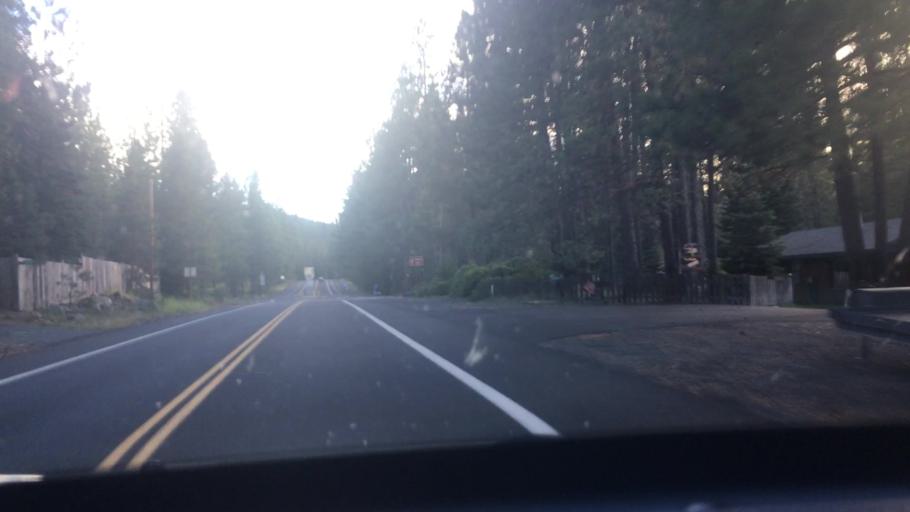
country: US
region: Oregon
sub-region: Deschutes County
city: Deschutes River Woods
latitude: 44.0338
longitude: -121.5106
